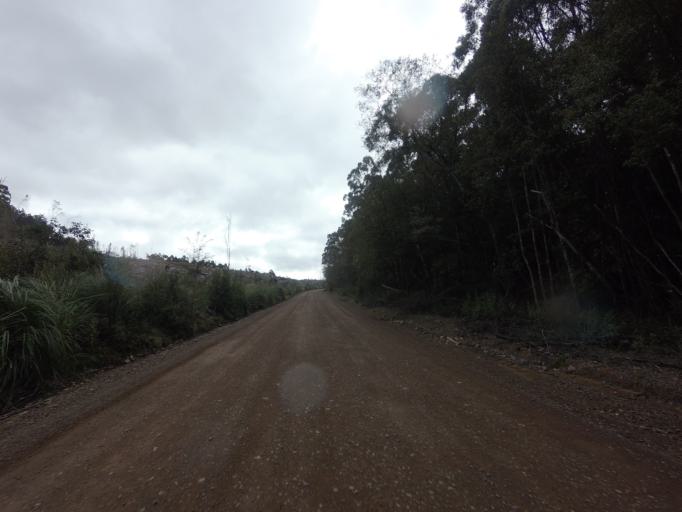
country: AU
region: Tasmania
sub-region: Huon Valley
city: Geeveston
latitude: -43.4900
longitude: 146.8876
